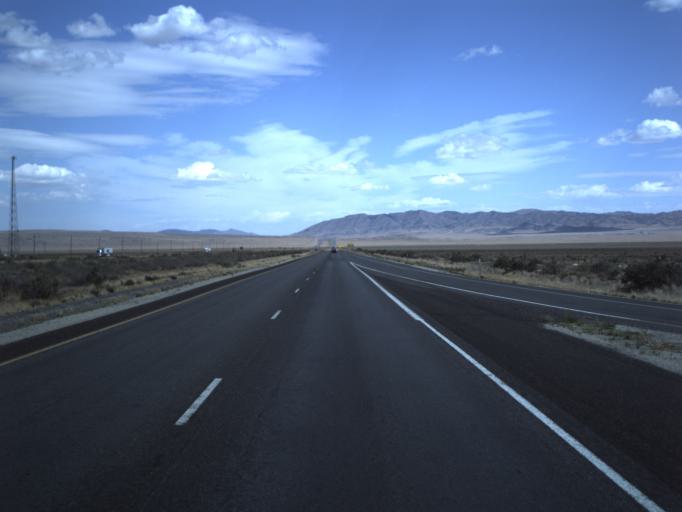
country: US
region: Utah
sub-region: Tooele County
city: Grantsville
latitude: 40.7331
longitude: -113.1078
